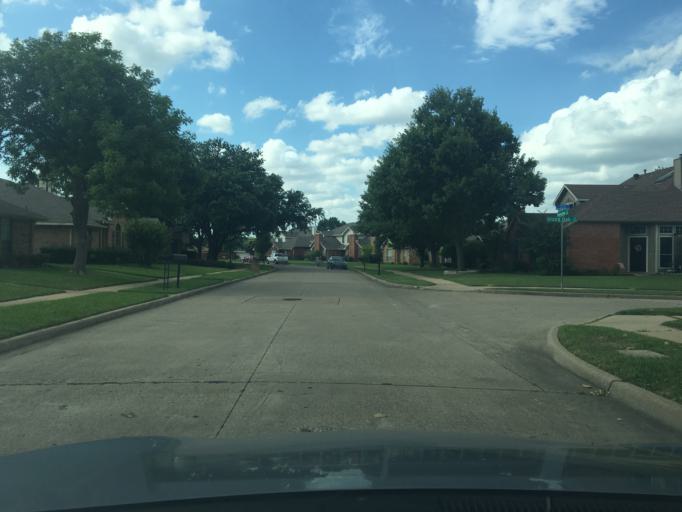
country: US
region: Texas
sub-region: Dallas County
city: Garland
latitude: 32.9322
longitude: -96.6767
